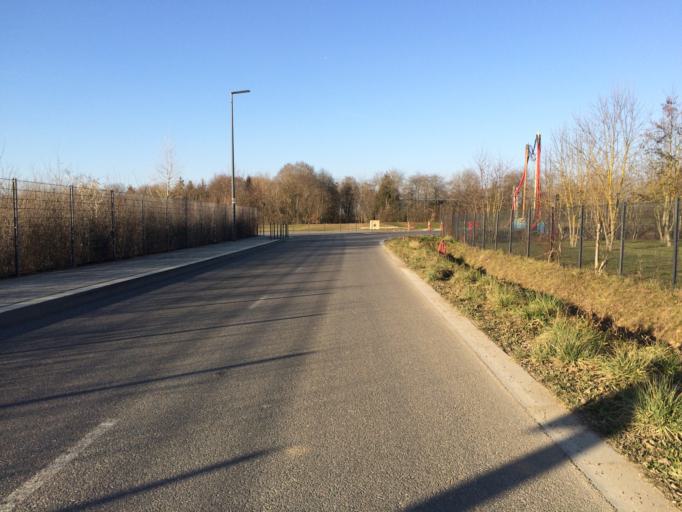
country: FR
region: Ile-de-France
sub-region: Departement de l'Essonne
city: Vauhallan
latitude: 48.7181
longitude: 2.1990
